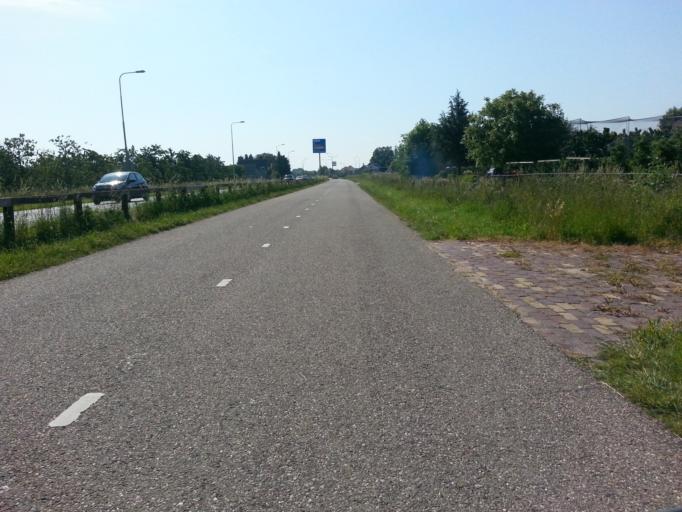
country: NL
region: Utrecht
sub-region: Gemeente Wijk bij Duurstede
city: Wijk bij Duurstede
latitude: 51.9888
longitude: 5.3297
